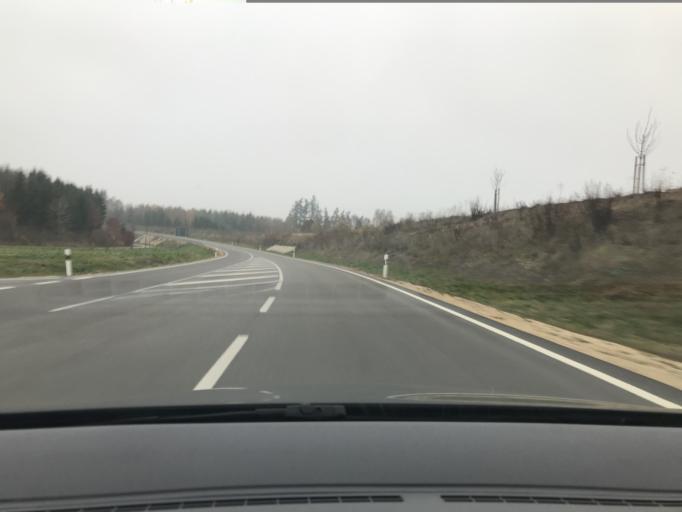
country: DE
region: Bavaria
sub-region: Swabia
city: Fremdingen
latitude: 48.9654
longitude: 10.4506
